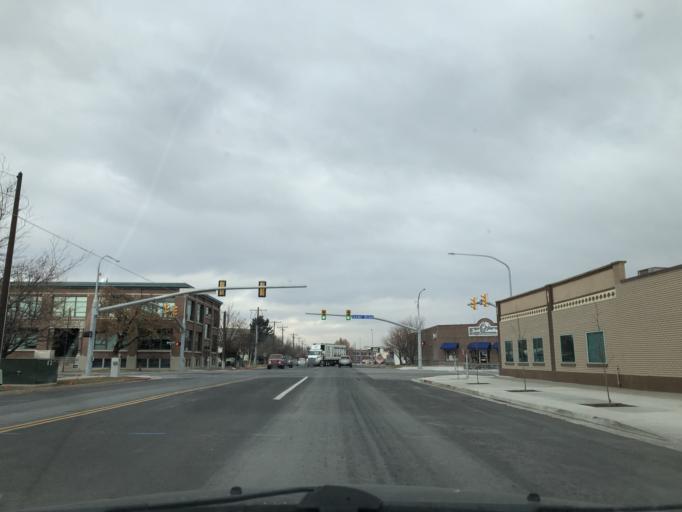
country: US
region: Utah
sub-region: Cache County
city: Logan
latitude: 41.7309
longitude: -111.8376
